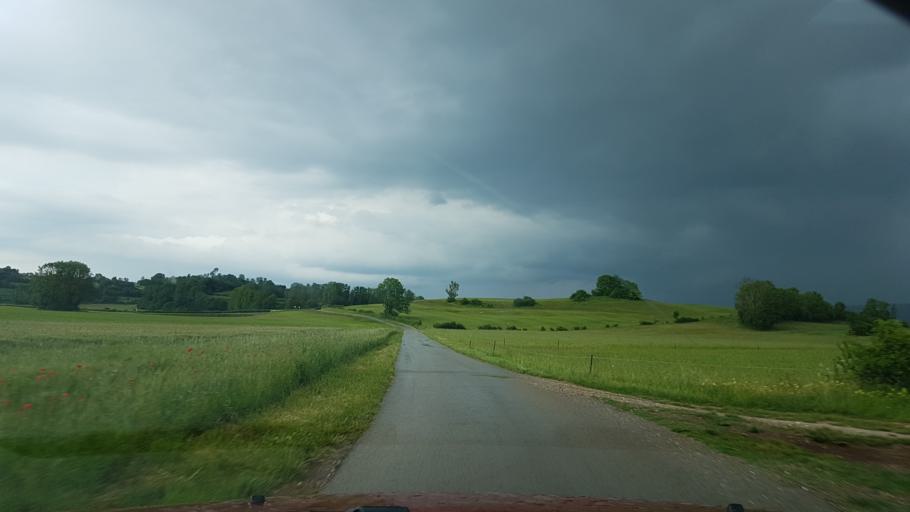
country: FR
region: Franche-Comte
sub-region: Departement du Jura
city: Clairvaux-les-Lacs
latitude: 46.5326
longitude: 5.7260
